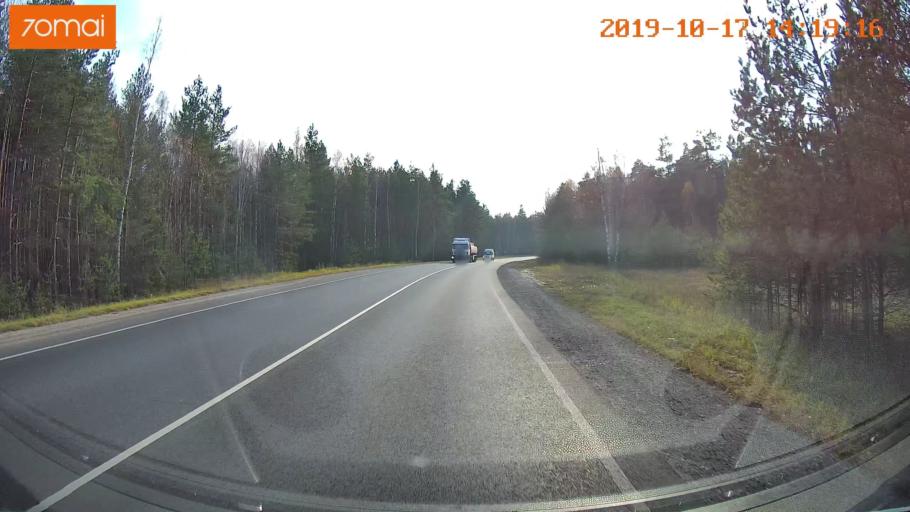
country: RU
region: Rjazan
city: Spas-Klepiki
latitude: 55.0521
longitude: 40.0231
